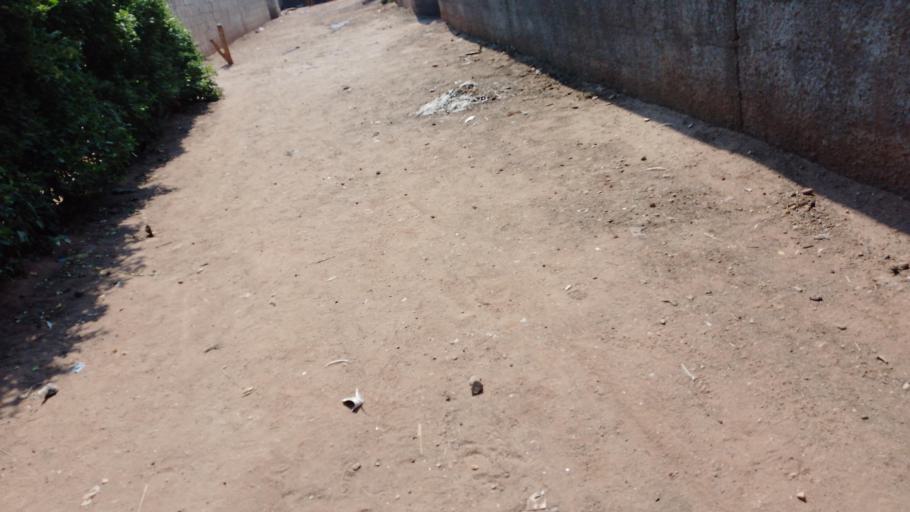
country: ZM
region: Lusaka
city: Lusaka
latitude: -15.3972
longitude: 28.3710
